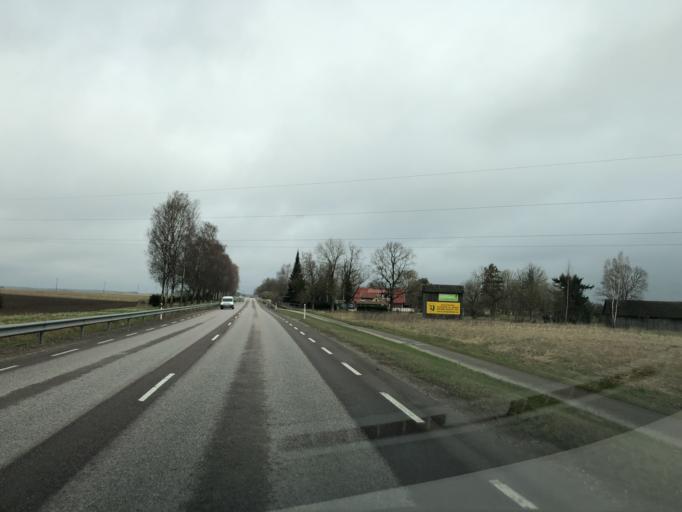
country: EE
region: Jogevamaa
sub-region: Jogeva linn
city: Jogeva
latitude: 58.7253
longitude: 26.3912
